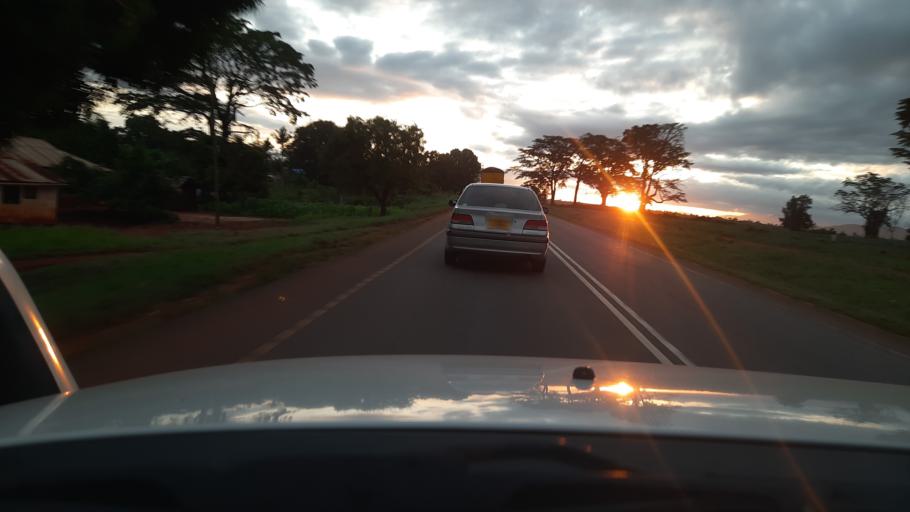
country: TZ
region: Tanga
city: Muheza
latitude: -5.1421
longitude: 38.8639
